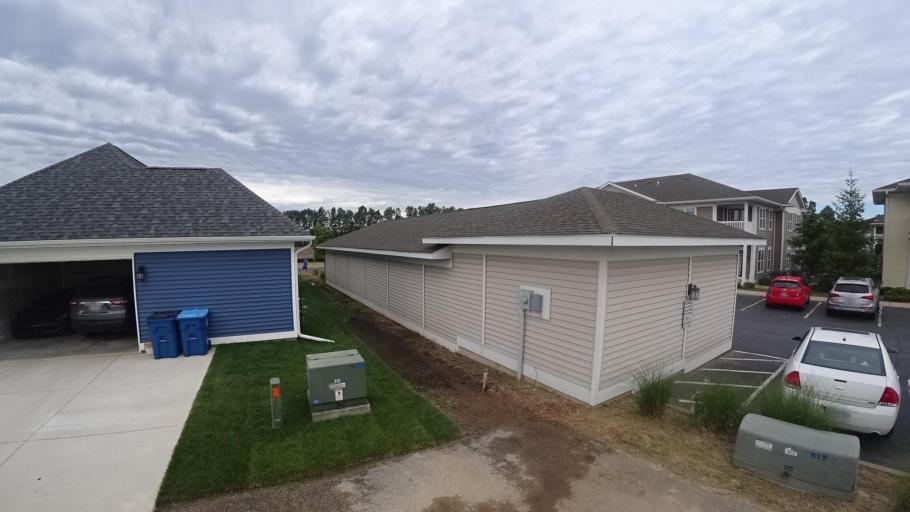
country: US
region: Indiana
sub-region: Porter County
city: Burns Harbor
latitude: 41.6040
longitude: -87.1323
